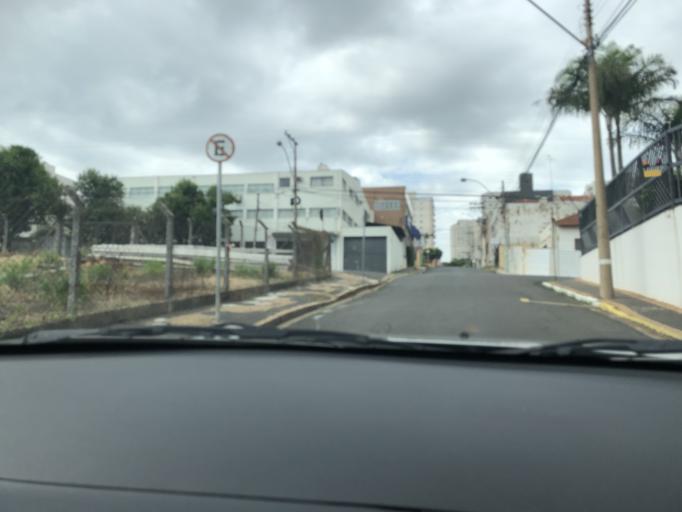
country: BR
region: Sao Paulo
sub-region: Americana
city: Americana
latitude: -22.7363
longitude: -47.3352
